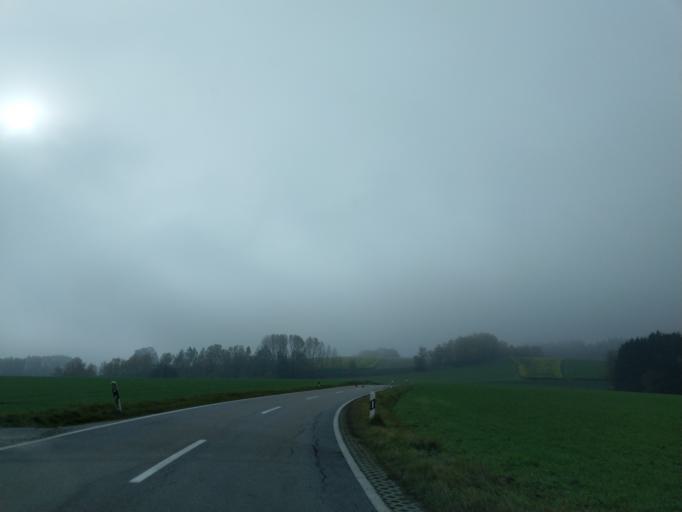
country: DE
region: Bavaria
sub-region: Lower Bavaria
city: Schollnach
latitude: 48.7761
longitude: 13.1705
